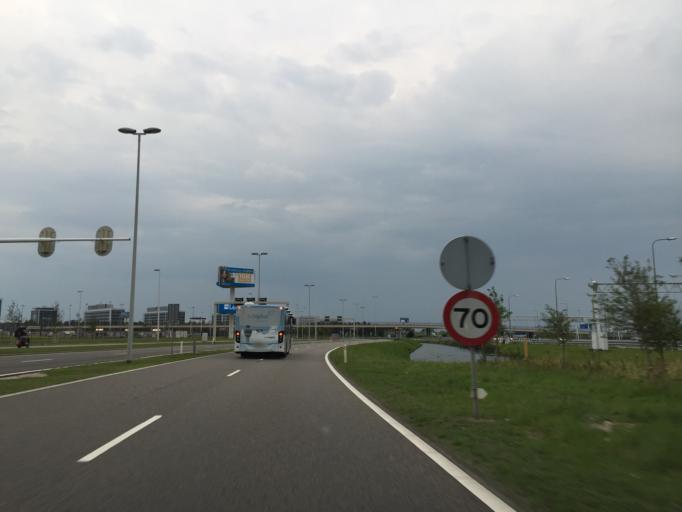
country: NL
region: North Holland
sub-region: Gemeente Aalsmeer
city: Aalsmeer
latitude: 52.3125
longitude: 4.7511
